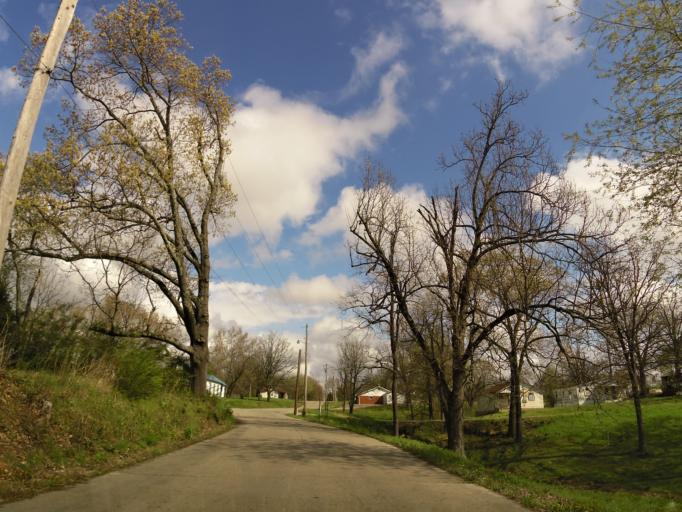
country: US
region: Missouri
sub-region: Butler County
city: Poplar Bluff
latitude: 36.7667
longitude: -90.3972
